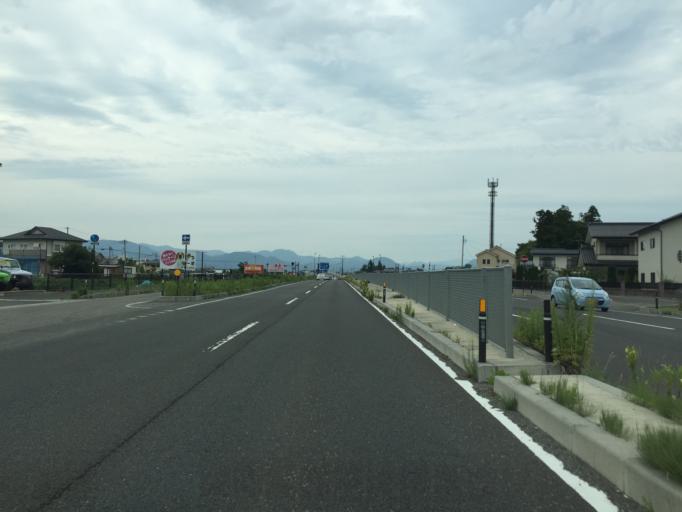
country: JP
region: Fukushima
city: Fukushima-shi
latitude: 37.7343
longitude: 140.4416
